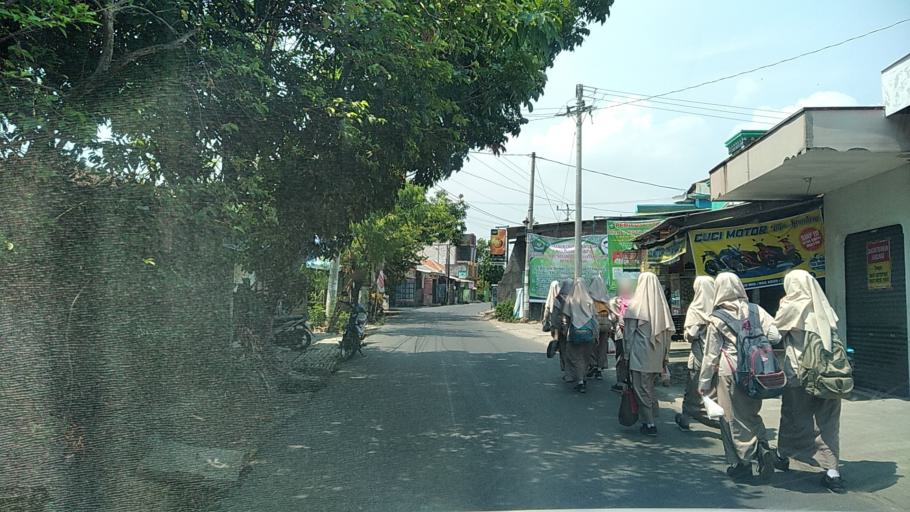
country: ID
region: Central Java
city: Mranggen
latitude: -7.0164
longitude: 110.4836
